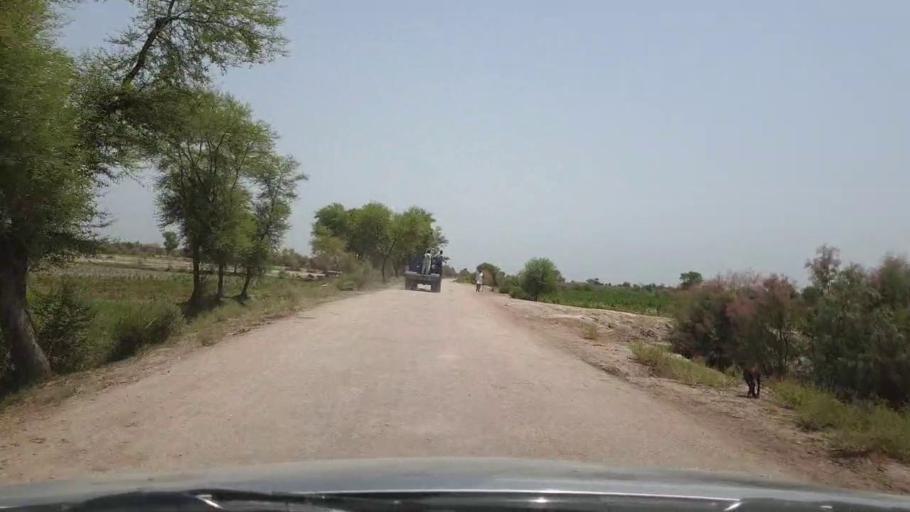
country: PK
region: Sindh
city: Pano Aqil
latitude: 27.8731
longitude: 69.1583
